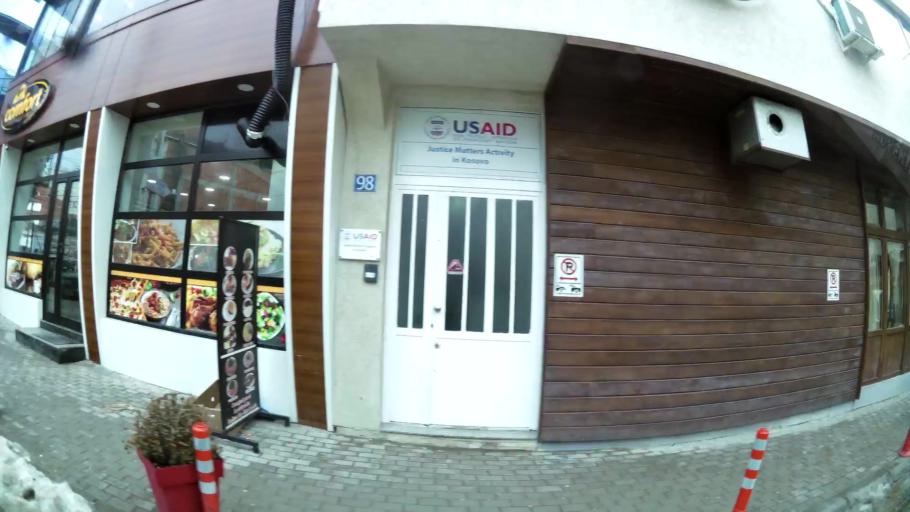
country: XK
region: Pristina
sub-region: Komuna e Prishtines
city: Pristina
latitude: 42.6651
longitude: 21.1626
